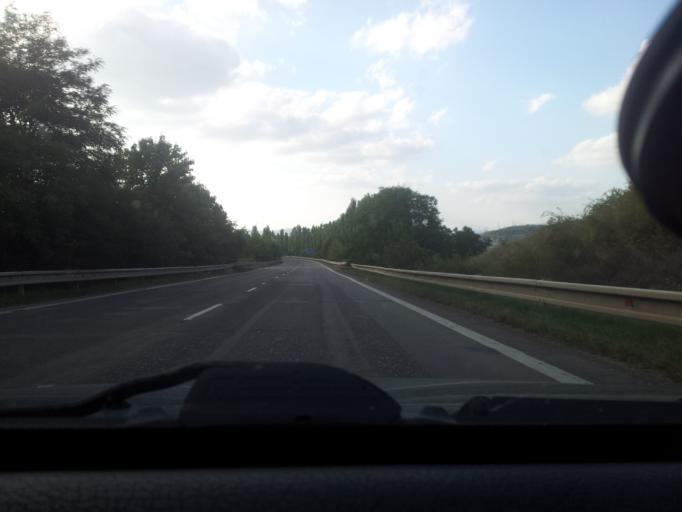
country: SK
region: Nitriansky
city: Levice
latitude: 48.2269
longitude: 18.6097
